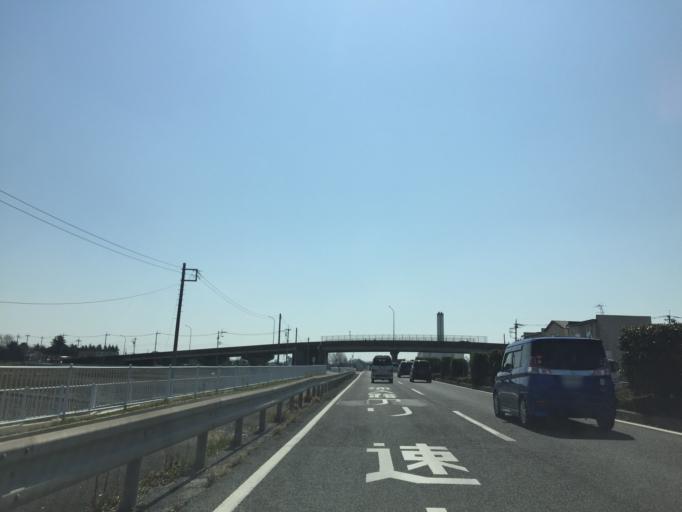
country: JP
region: Saitama
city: Kamifukuoka
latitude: 35.8715
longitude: 139.5417
